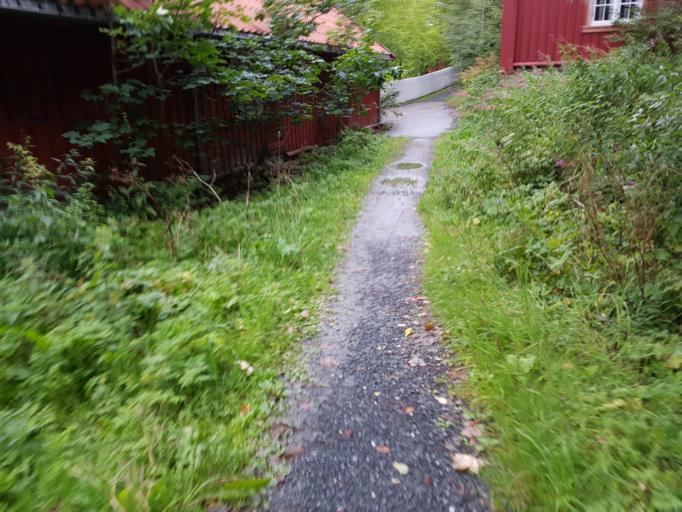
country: NO
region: Sor-Trondelag
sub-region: Trondheim
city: Trondheim
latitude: 63.4069
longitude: 10.4812
